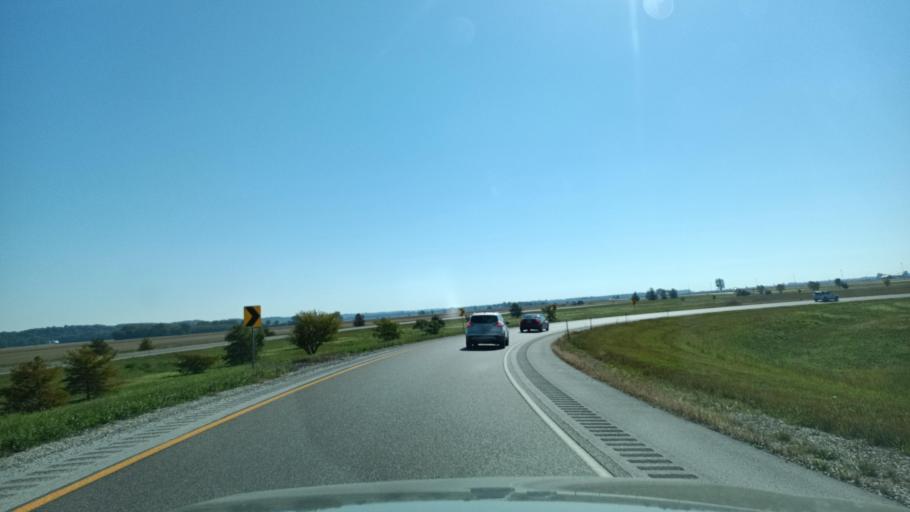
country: US
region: Missouri
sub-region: Marion County
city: Hannibal
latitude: 39.7563
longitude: -91.2951
